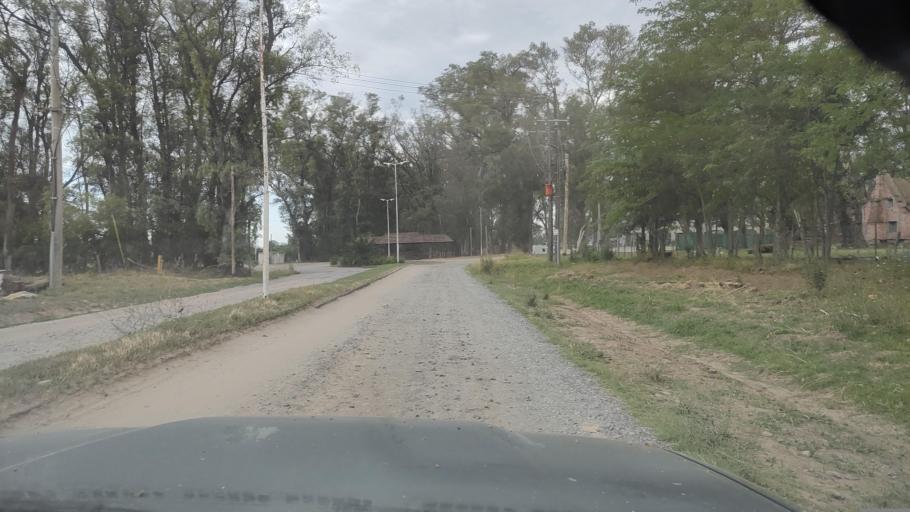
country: AR
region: Buenos Aires
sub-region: Partido de Lujan
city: Lujan
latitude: -34.5457
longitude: -59.0781
